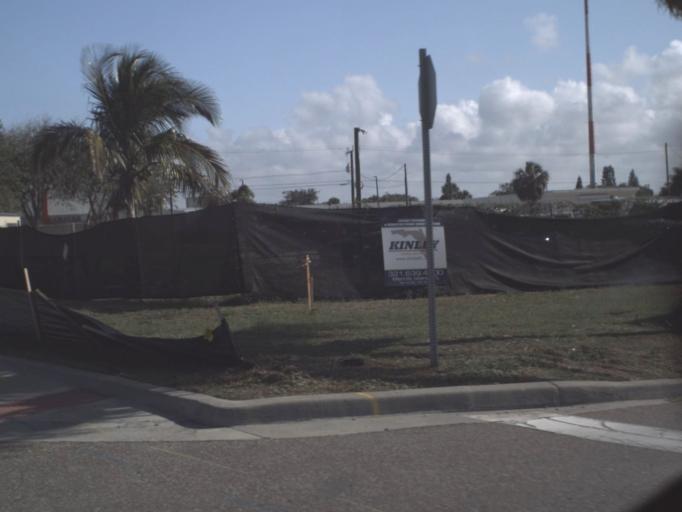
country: US
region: Florida
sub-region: Brevard County
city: Melbourne
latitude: 28.0903
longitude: -80.6084
